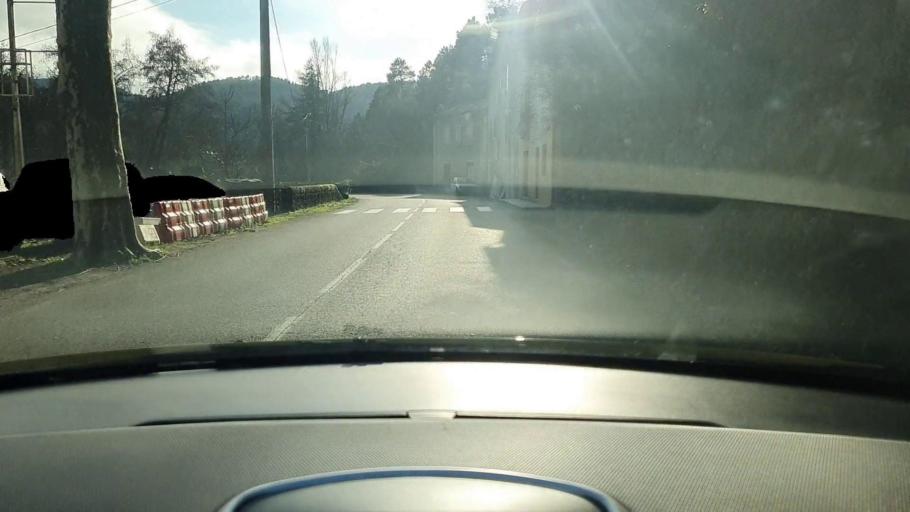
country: FR
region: Languedoc-Roussillon
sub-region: Departement du Gard
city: Branoux-les-Taillades
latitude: 44.3019
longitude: 3.9765
